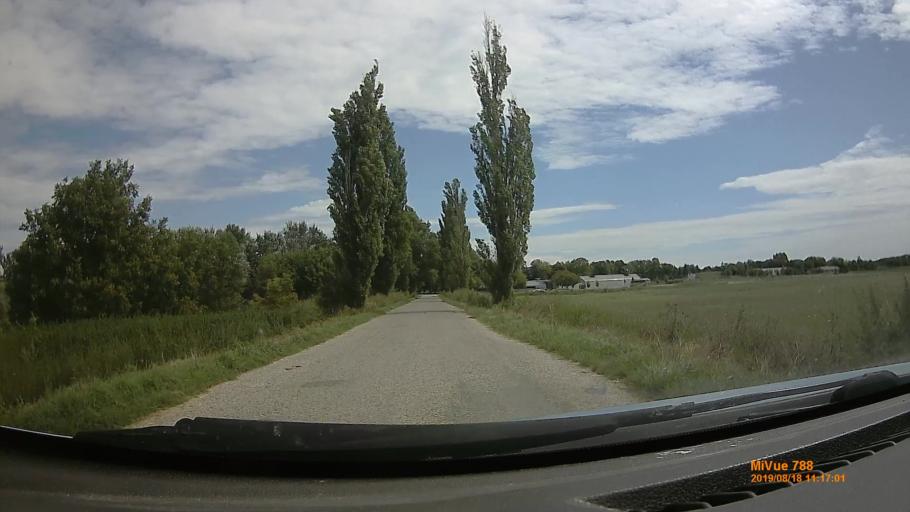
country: HU
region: Fejer
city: Szabadbattyan
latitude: 47.0884
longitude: 18.4174
